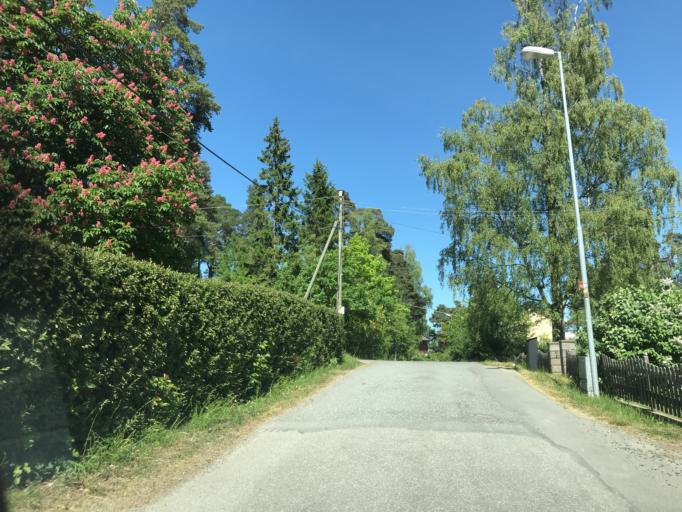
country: SE
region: Stockholm
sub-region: Sollentuna Kommun
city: Sollentuna
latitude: 59.4196
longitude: 17.9757
